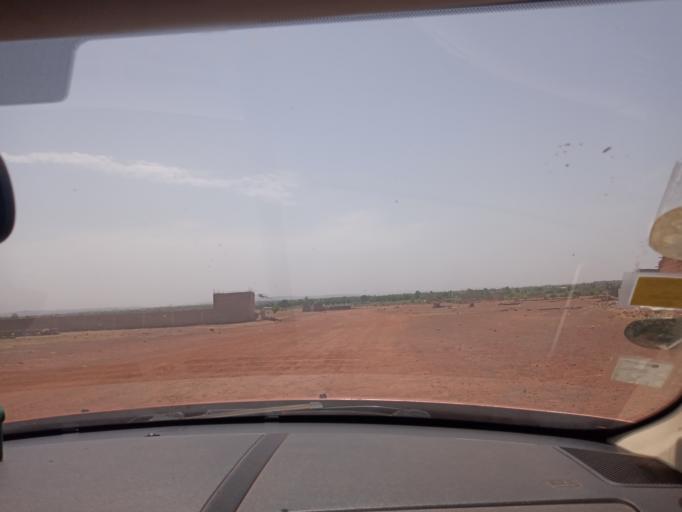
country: ML
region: Bamako
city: Bamako
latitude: 12.5190
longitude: -7.7921
